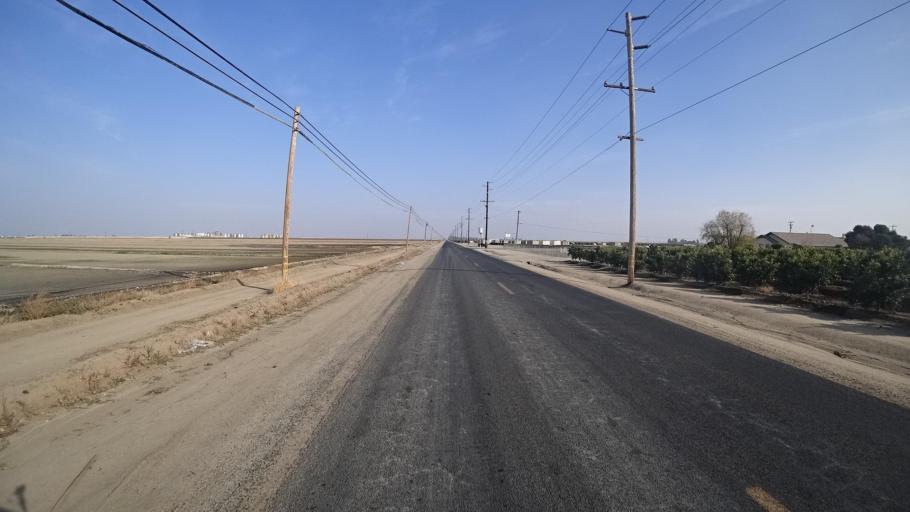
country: US
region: California
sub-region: Kern County
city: Delano
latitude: 35.7759
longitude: -119.2016
